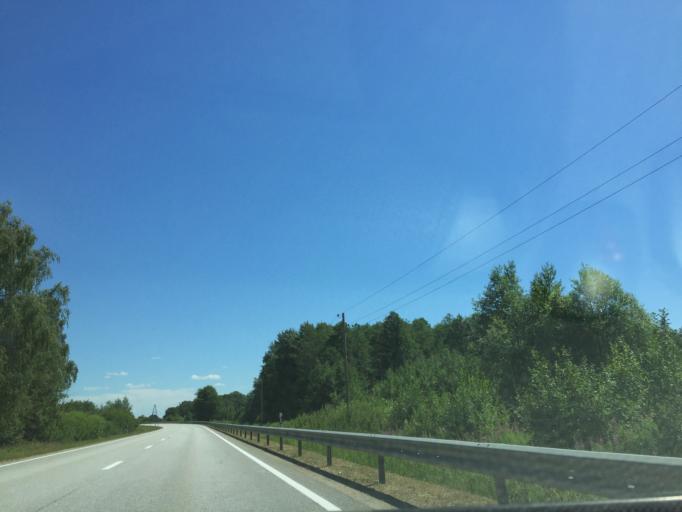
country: LV
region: Livani
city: Livani
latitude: 56.5344
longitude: 26.2893
